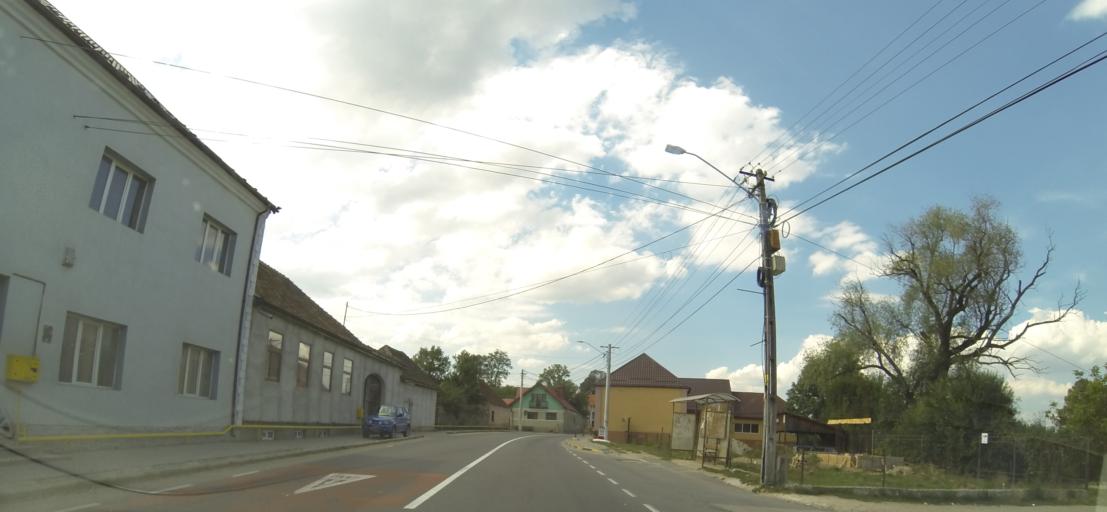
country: RO
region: Brasov
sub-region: Comuna Sinca Veche
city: Persani
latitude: 45.7812
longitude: 25.2112
